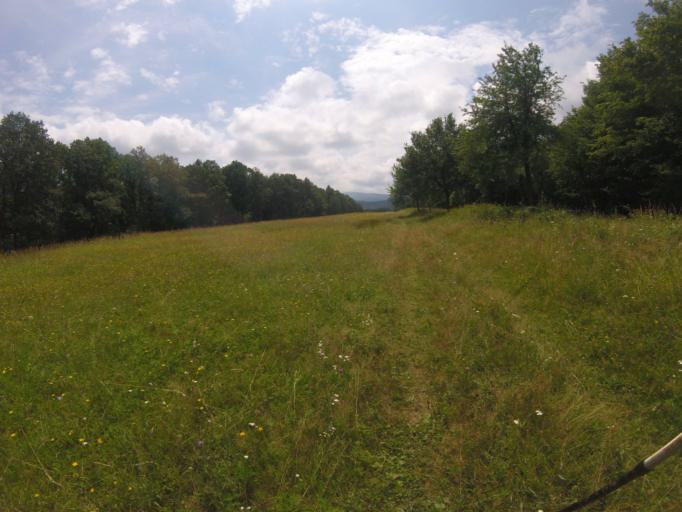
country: SK
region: Nitriansky
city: Sahy
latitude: 48.0207
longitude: 18.9624
